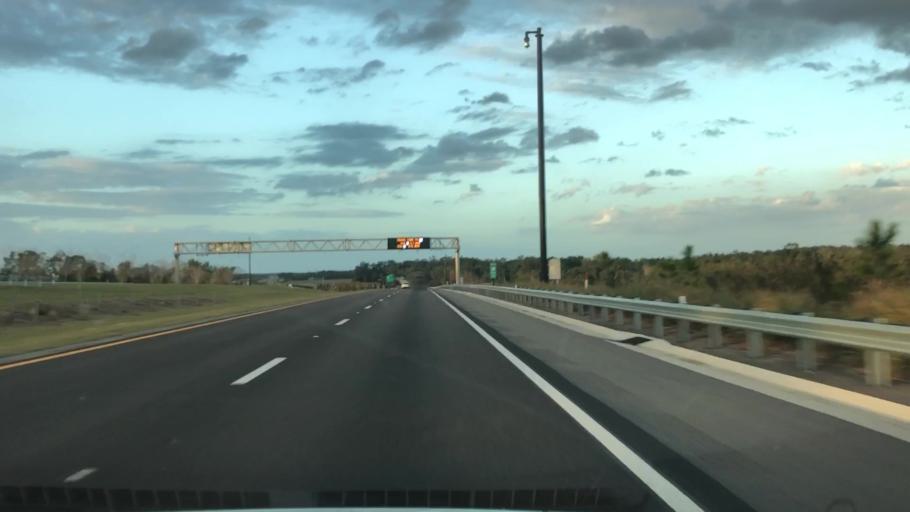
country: US
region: Florida
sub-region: Orange County
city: Zellwood
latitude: 28.7282
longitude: -81.5631
